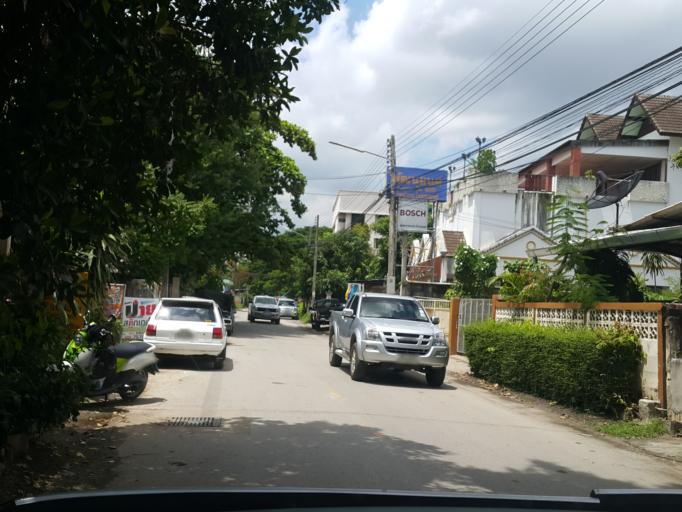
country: TH
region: Chiang Mai
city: Chiang Mai
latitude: 18.7890
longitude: 99.0111
